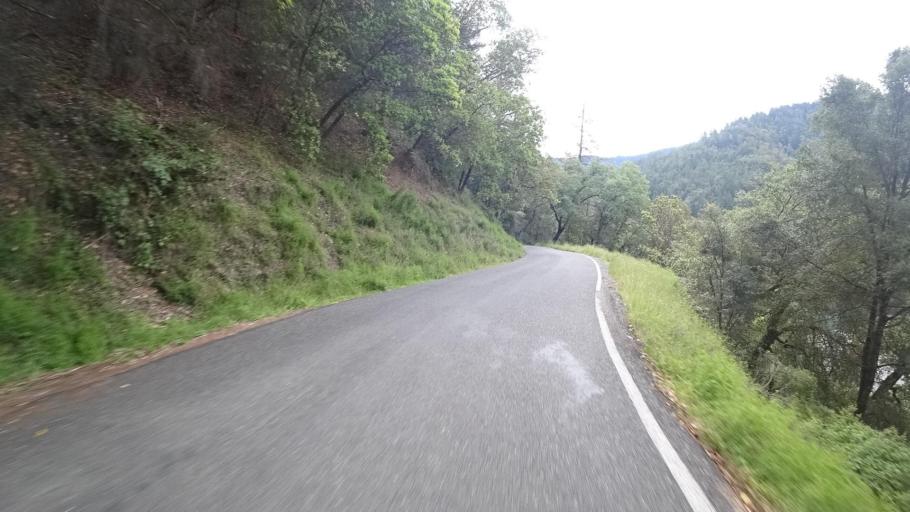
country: US
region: California
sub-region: Humboldt County
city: Willow Creek
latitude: 40.9498
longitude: -123.6148
